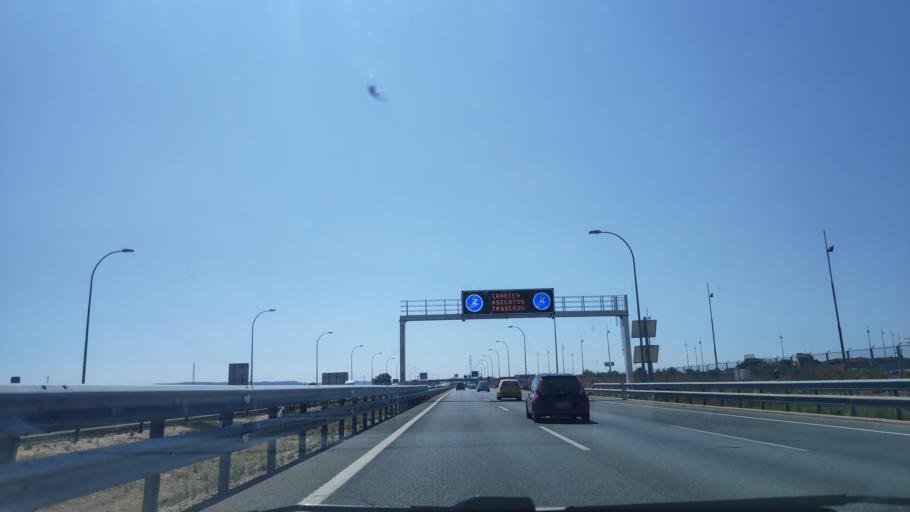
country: ES
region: Madrid
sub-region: Provincia de Madrid
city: Torrejon de la Calzada
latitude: 40.2076
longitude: -3.7911
